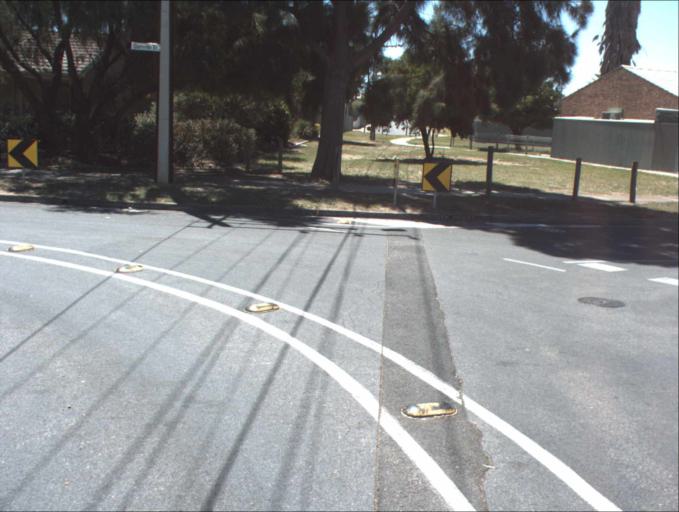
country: AU
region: South Australia
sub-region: Charles Sturt
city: West Lakes Shore
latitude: -34.8505
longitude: 138.4934
